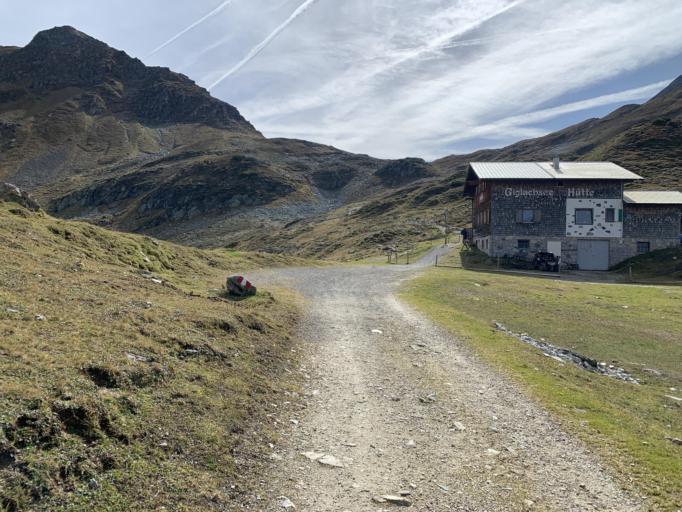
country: AT
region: Salzburg
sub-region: Politischer Bezirk Tamsweg
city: Tweng
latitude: 47.2800
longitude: 13.6382
